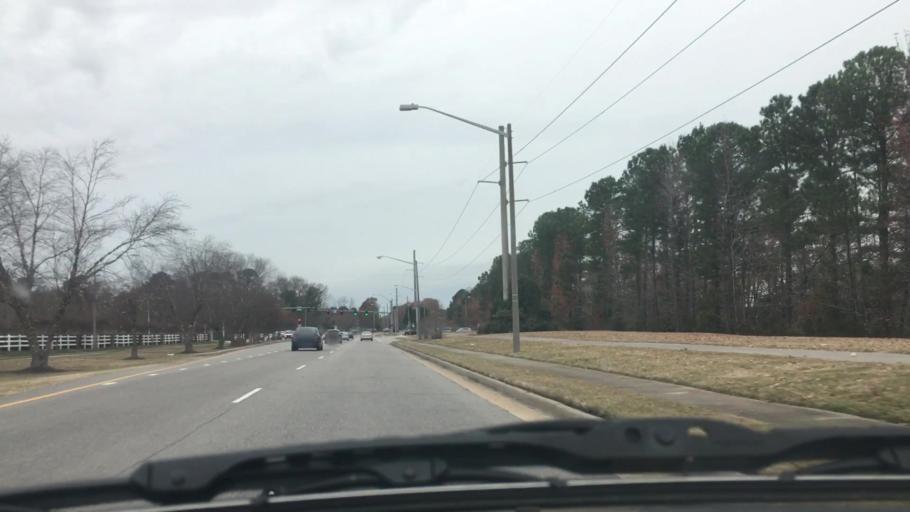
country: US
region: Virginia
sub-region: City of Virginia Beach
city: Virginia Beach
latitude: 36.8119
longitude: -76.1234
